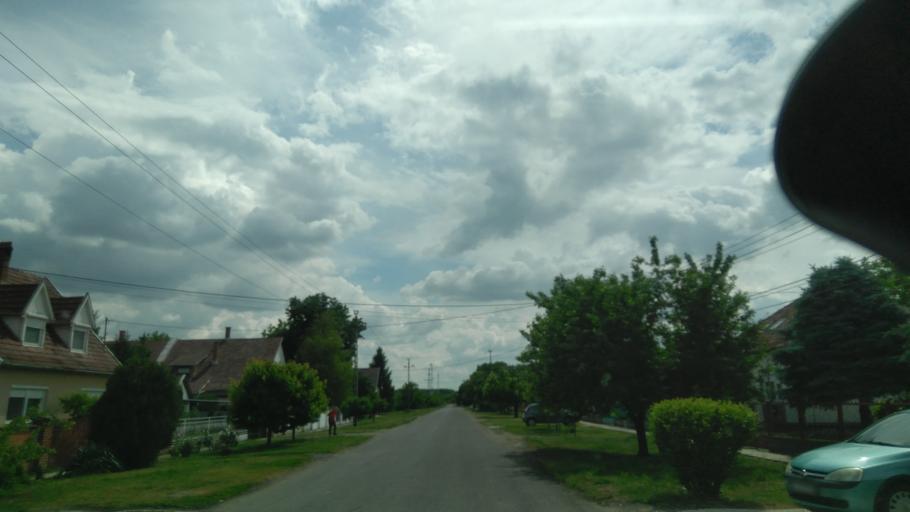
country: HU
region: Bekes
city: Mezohegyes
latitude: 46.3187
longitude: 20.8072
